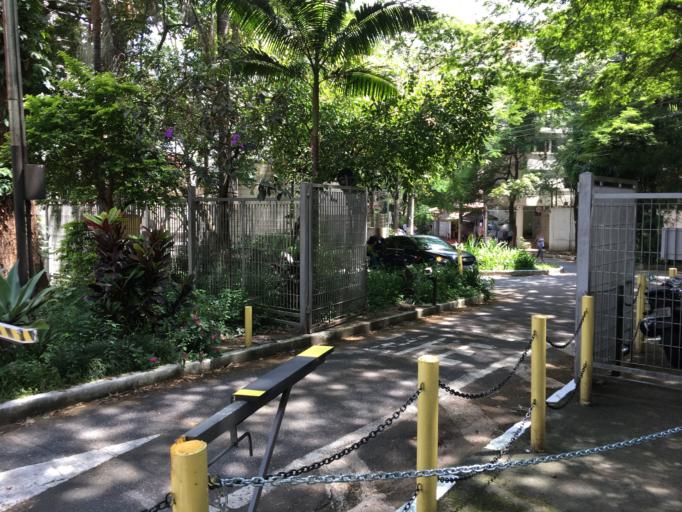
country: BR
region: Sao Paulo
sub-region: Sao Paulo
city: Sao Paulo
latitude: -23.5575
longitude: -46.6728
